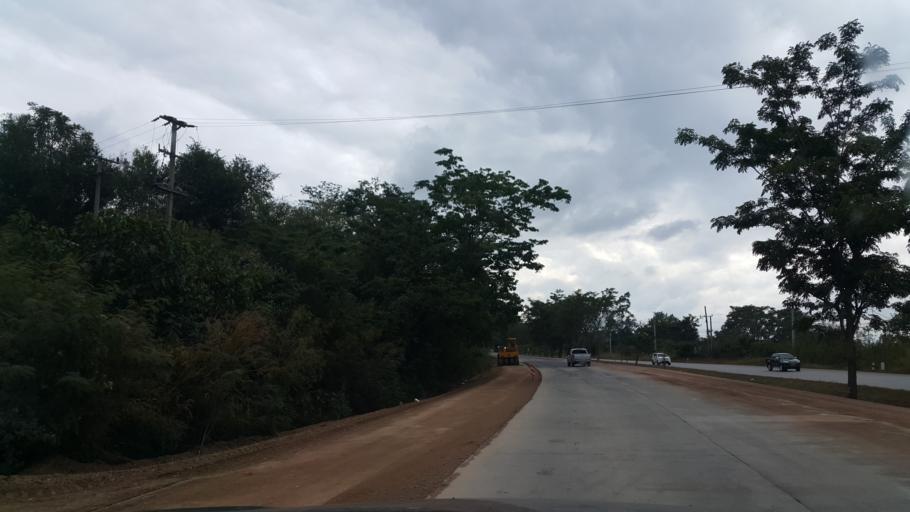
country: TH
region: Lampang
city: Ko Kha
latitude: 18.1414
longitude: 99.3910
